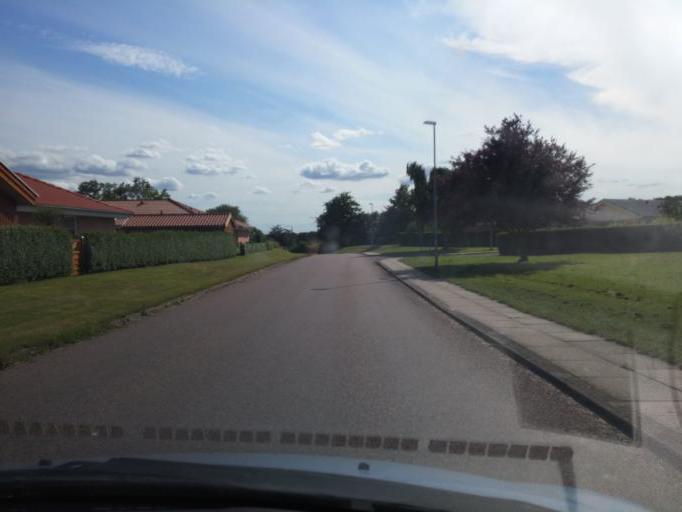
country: DK
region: South Denmark
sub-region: Kerteminde Kommune
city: Munkebo
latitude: 55.4662
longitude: 10.5647
